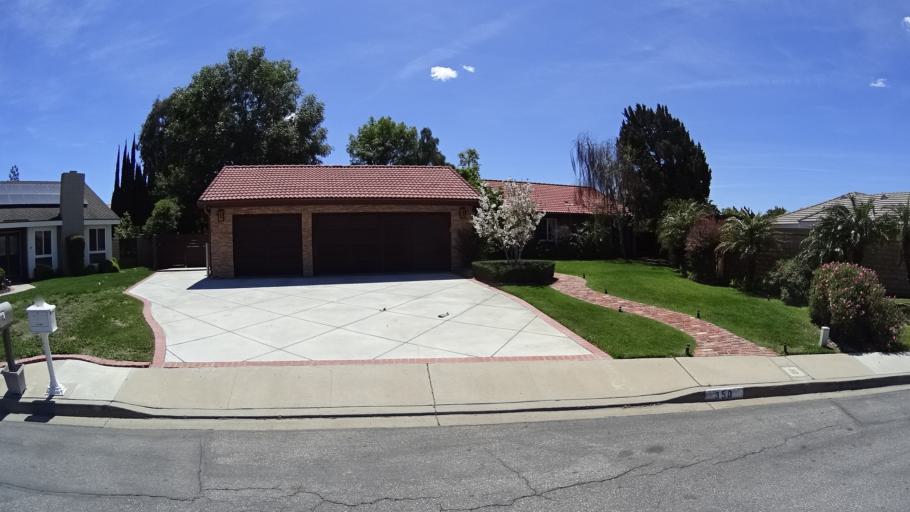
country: US
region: California
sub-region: Ventura County
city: Thousand Oaks
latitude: 34.2198
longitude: -118.8699
